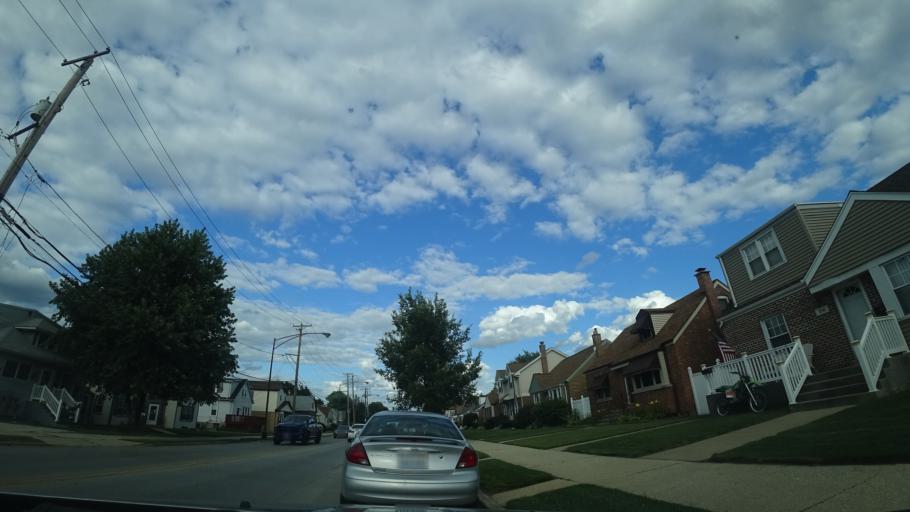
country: US
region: Illinois
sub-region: Cook County
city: Merrionette Park
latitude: 41.6841
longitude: -87.7096
